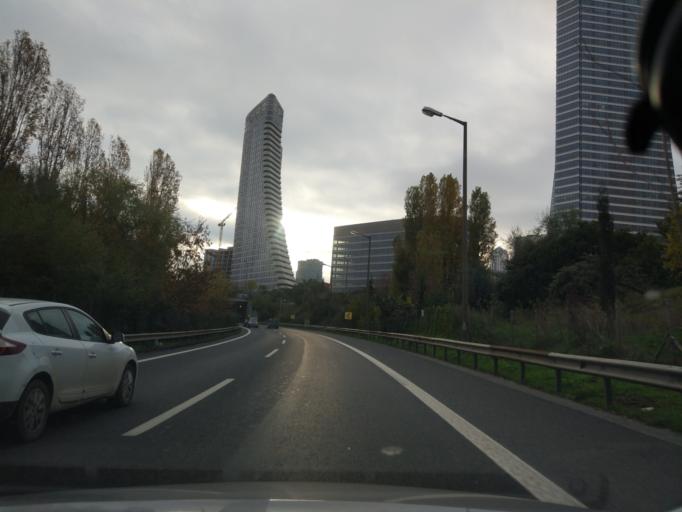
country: TR
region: Istanbul
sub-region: Atasehir
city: Atasehir
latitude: 40.9968
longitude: 29.1209
